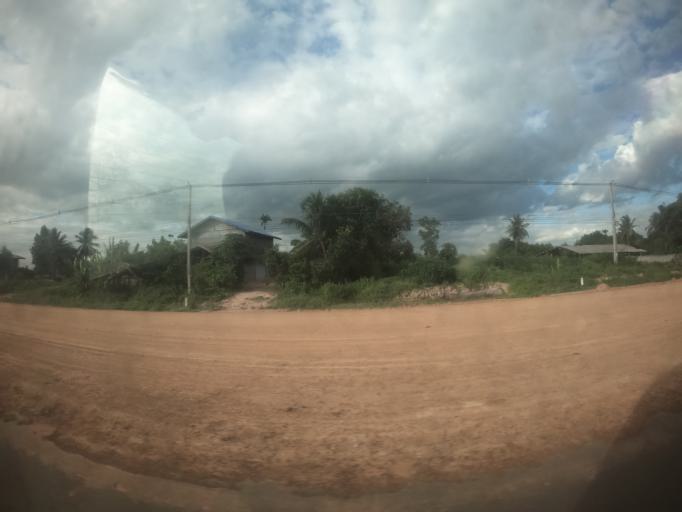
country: TH
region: Surin
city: Kap Choeng
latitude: 14.4918
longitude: 103.5729
